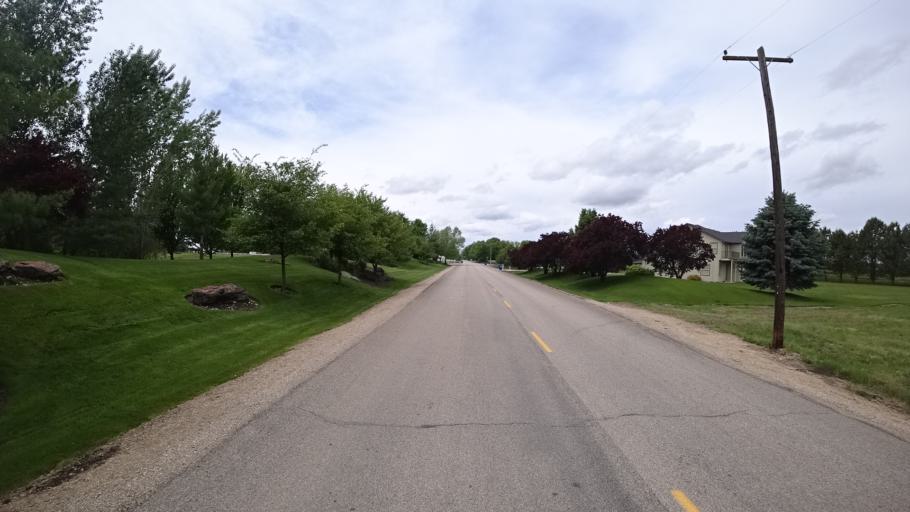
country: US
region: Idaho
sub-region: Ada County
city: Star
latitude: 43.6891
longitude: -116.4415
